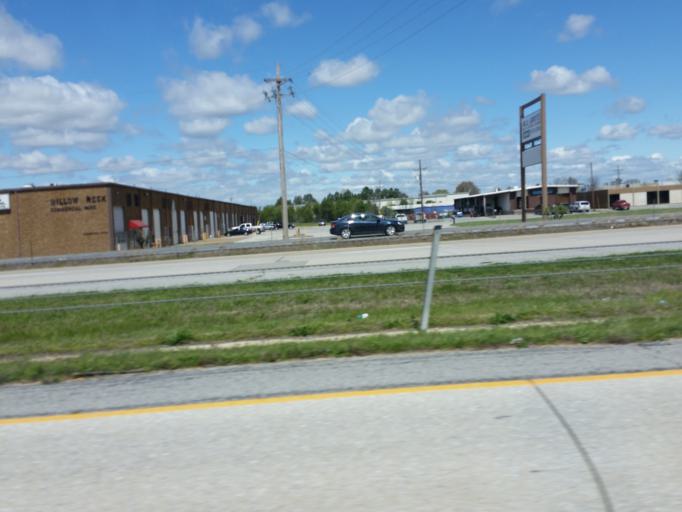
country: US
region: Arkansas
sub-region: Craighead County
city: Jonesboro
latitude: 35.8069
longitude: -90.6434
